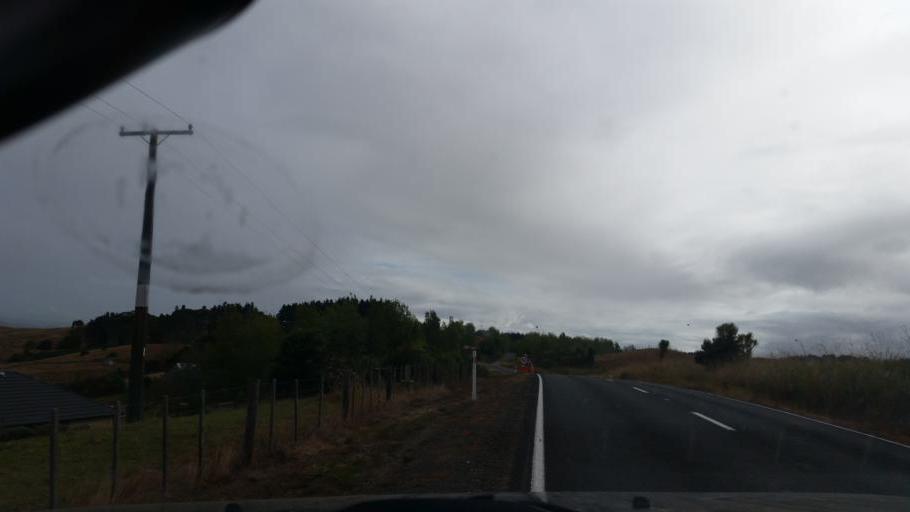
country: NZ
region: Auckland
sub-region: Auckland
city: Wellsford
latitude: -36.2168
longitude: 174.3892
